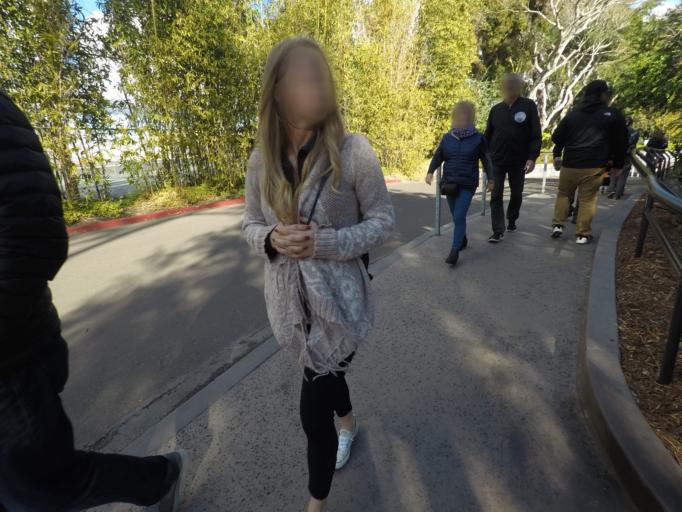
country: US
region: California
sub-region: San Diego County
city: San Diego
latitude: 32.7393
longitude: -117.1503
